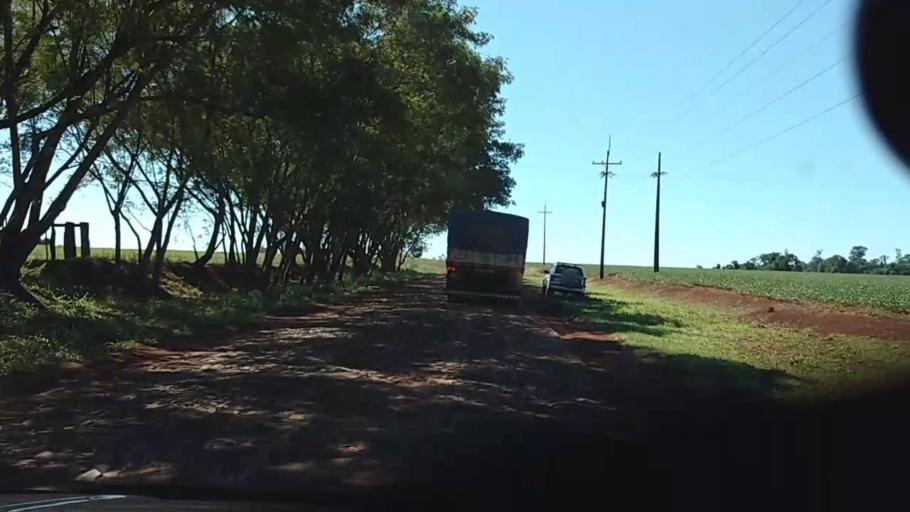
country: PY
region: Alto Parana
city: Naranjal
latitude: -25.9578
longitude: -55.1384
